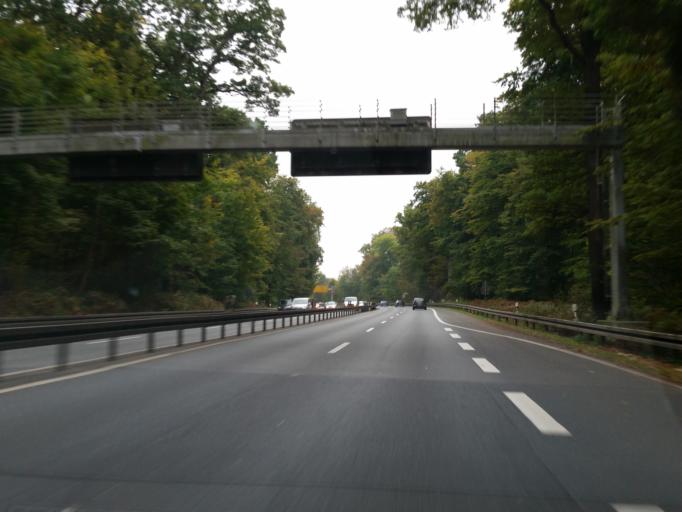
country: DE
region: Lower Saxony
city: Laatzen
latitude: 52.3583
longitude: 9.7847
